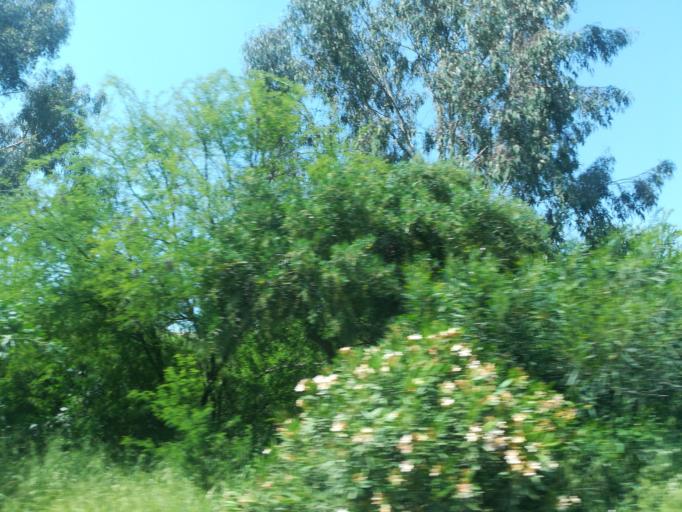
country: TR
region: Adana
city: Adana
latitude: 37.0249
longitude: 35.3627
